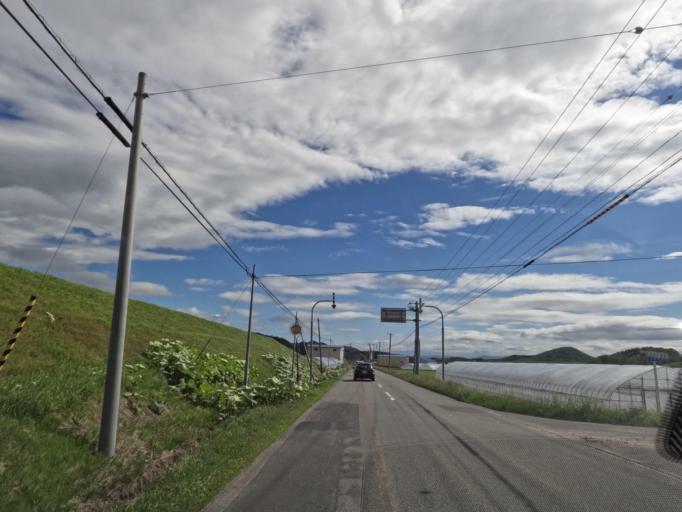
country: JP
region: Hokkaido
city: Kamikawa
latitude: 43.8578
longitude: 142.5591
